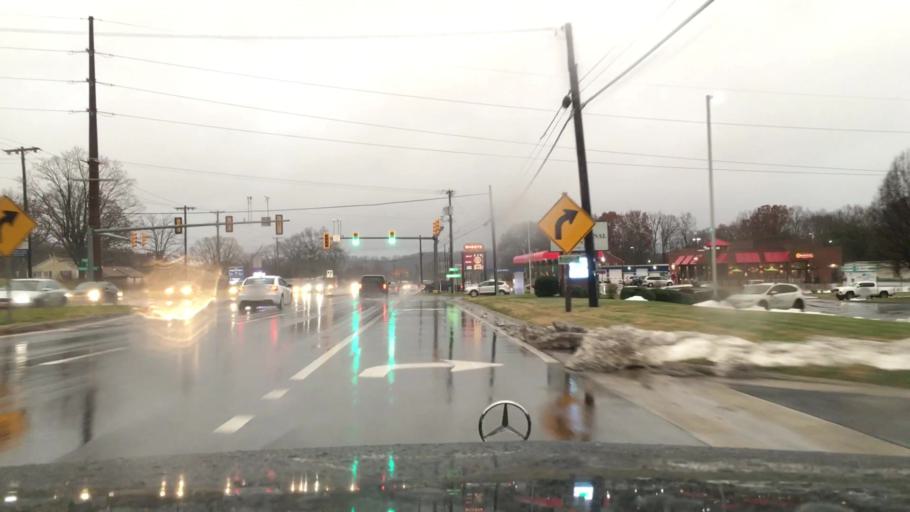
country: US
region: Virginia
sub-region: Campbell County
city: Timberlake
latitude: 37.3266
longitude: -79.1905
